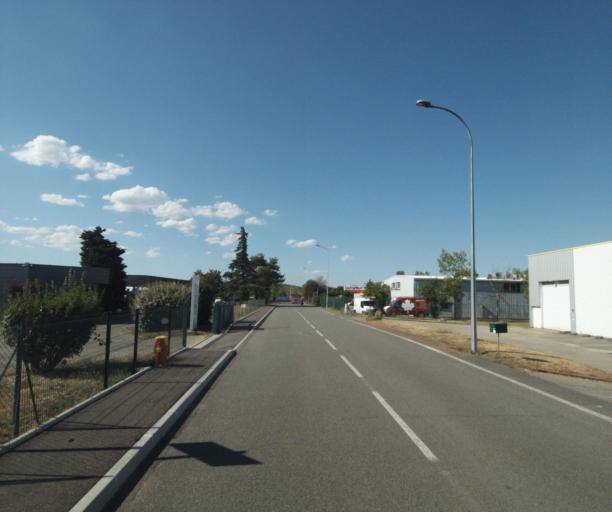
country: FR
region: Rhone-Alpes
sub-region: Departement du Rhone
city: Lentilly
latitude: 45.8179
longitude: 4.6860
